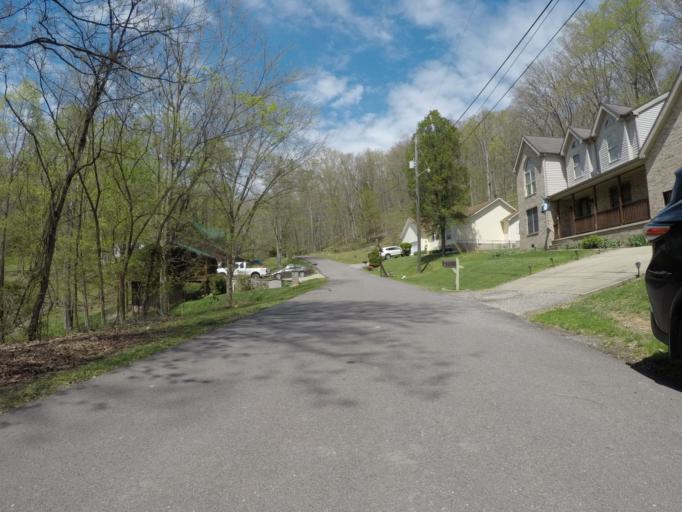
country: US
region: Ohio
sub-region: Lawrence County
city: Burlington
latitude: 38.3742
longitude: -82.5126
